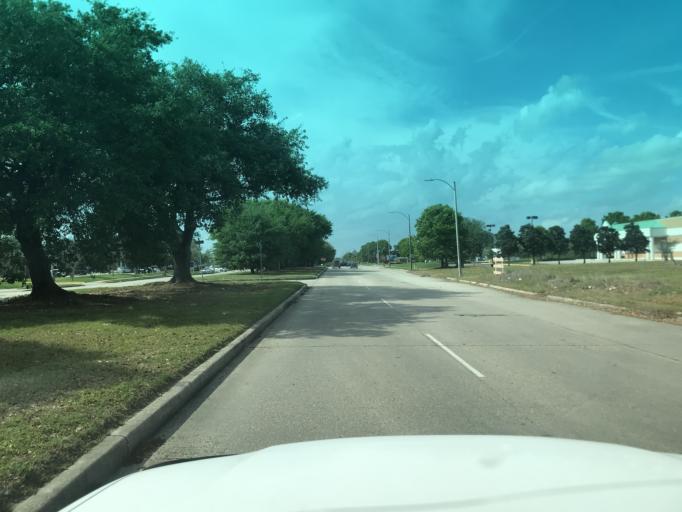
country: US
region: Louisiana
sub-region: Saint Bernard Parish
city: Chalmette
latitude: 30.0376
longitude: -89.9539
